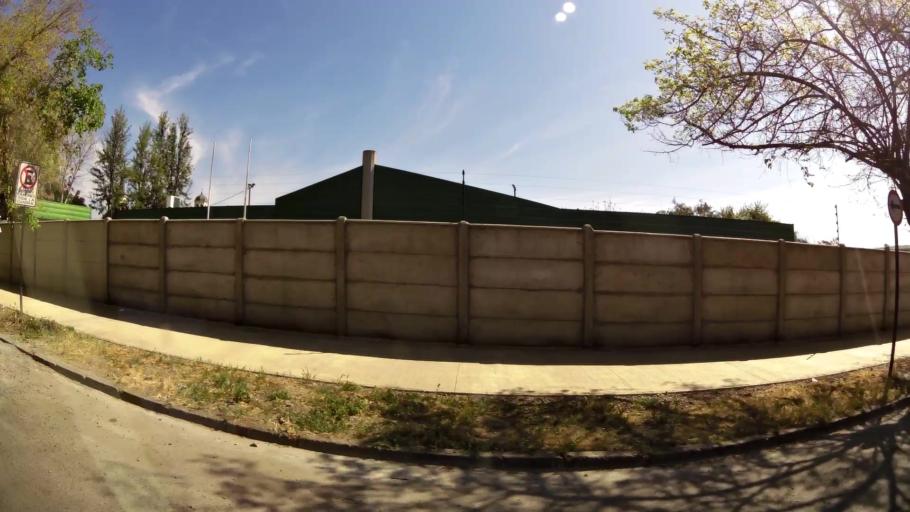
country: CL
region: Santiago Metropolitan
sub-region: Provincia de Santiago
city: Santiago
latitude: -33.4252
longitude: -70.6593
